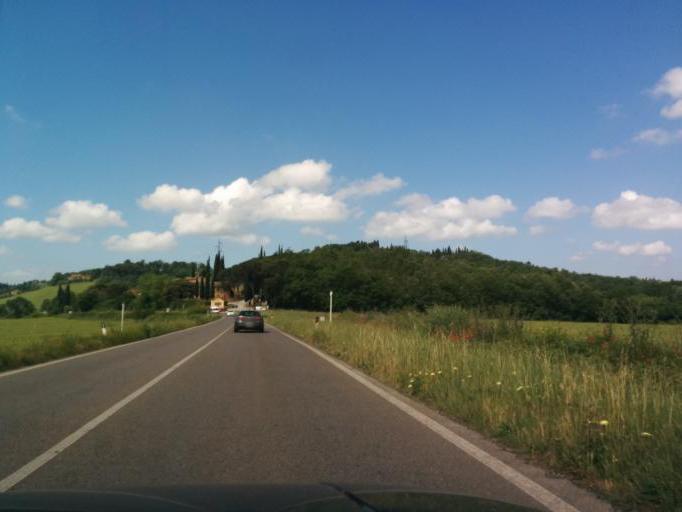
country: IT
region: Tuscany
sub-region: Provincia di Siena
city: Poggibonsi
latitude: 43.4593
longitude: 11.0958
